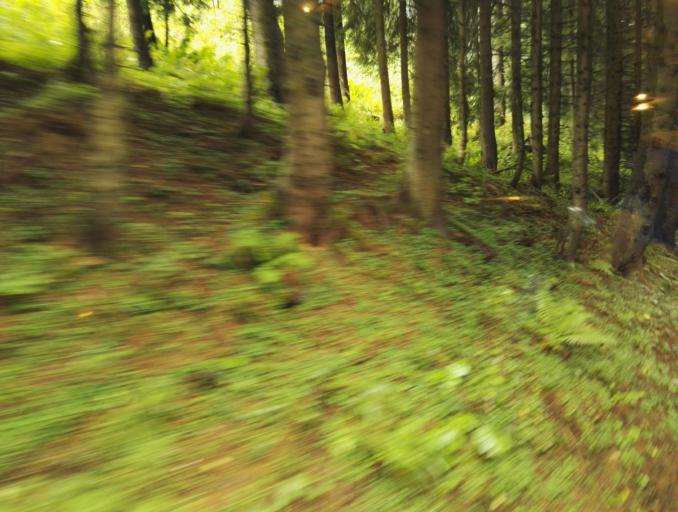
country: AT
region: Styria
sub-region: Politischer Bezirk Leoben
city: Eisenerz
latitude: 47.5266
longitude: 14.9427
